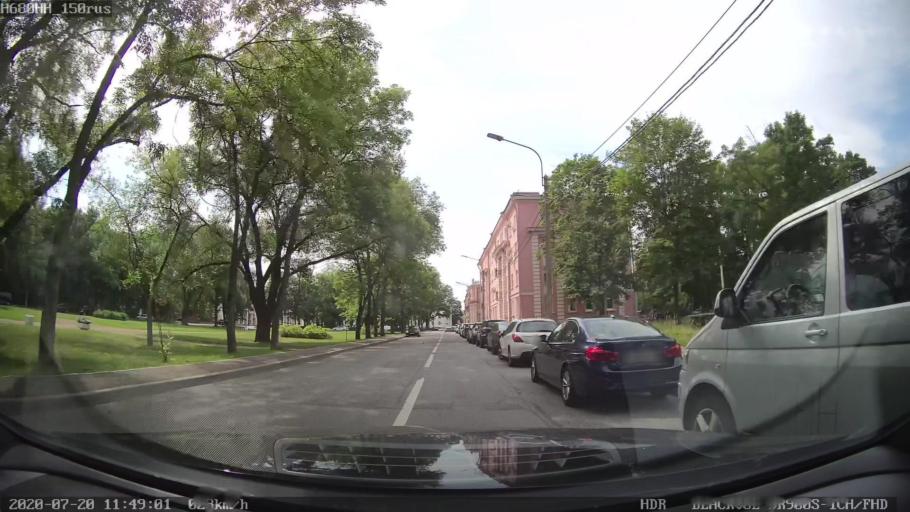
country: RU
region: St.-Petersburg
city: Peterhof
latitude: 59.8805
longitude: 29.9204
